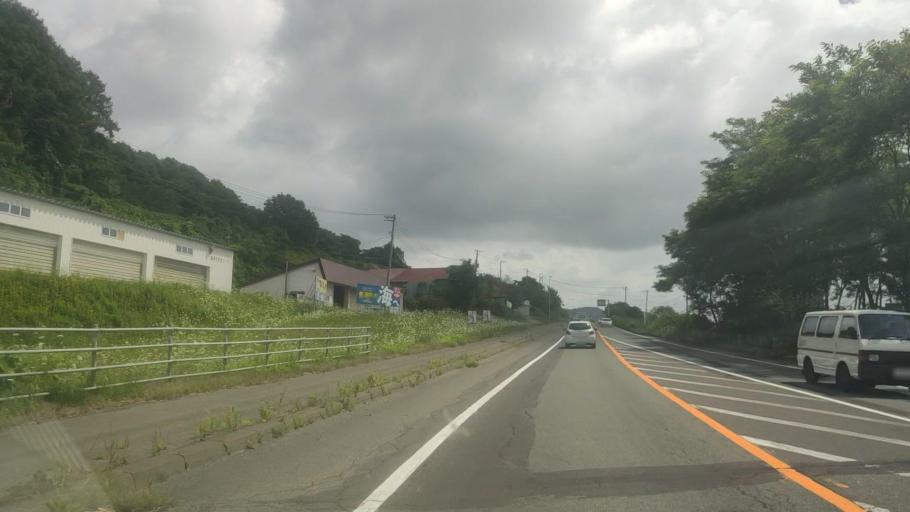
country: JP
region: Hokkaido
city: Niseko Town
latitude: 42.5889
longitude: 140.7058
